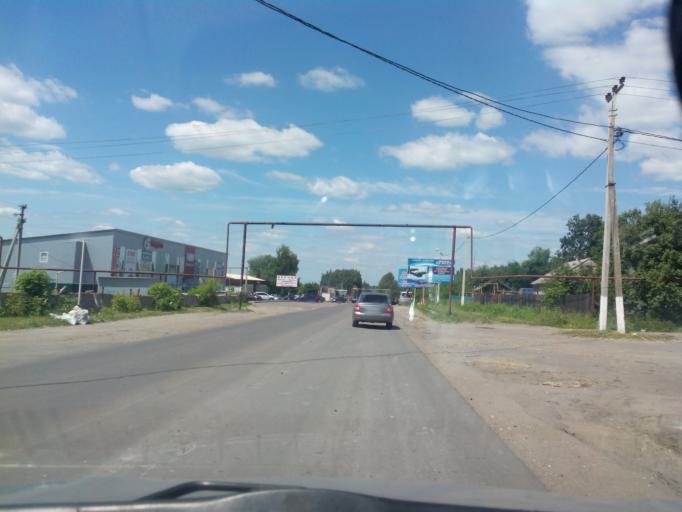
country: RU
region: Tambov
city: Zherdevka
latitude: 51.8185
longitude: 41.5084
